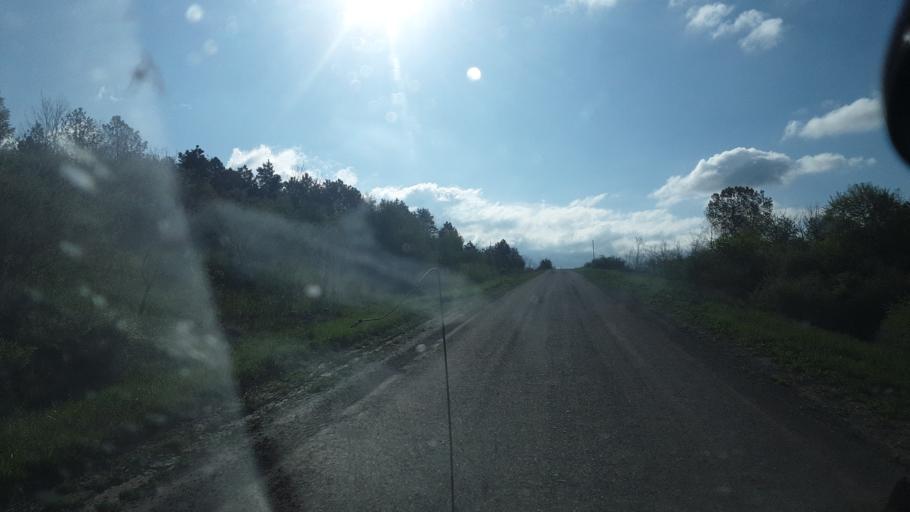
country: US
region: Ohio
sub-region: Noble County
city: Caldwell
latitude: 39.8130
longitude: -81.6653
